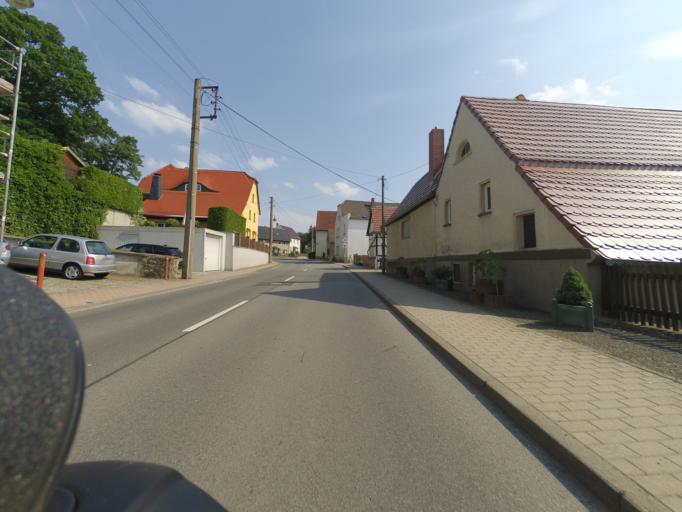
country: DE
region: Thuringia
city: Gerstenberg
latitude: 51.0290
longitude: 12.4412
